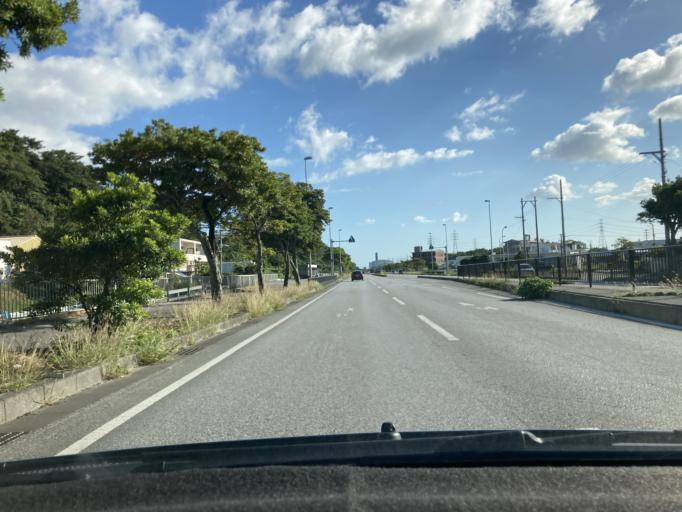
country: JP
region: Okinawa
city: Ishikawa
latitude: 26.4125
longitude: 127.8186
